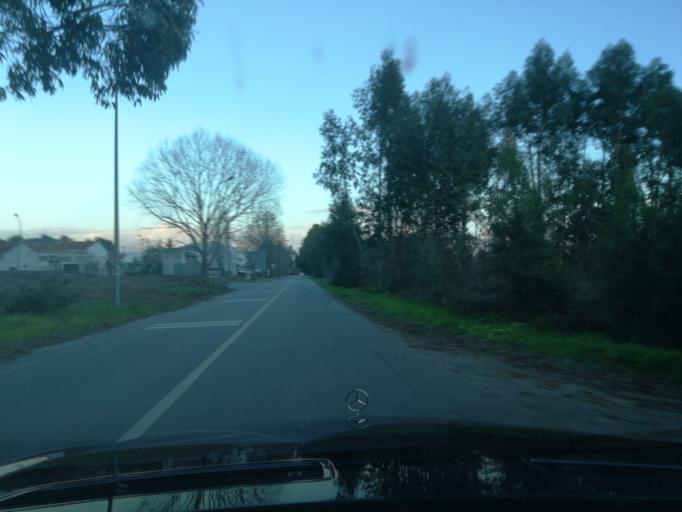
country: PT
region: Aveiro
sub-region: Estarreja
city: Estarreja
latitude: 40.7578
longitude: -8.5943
